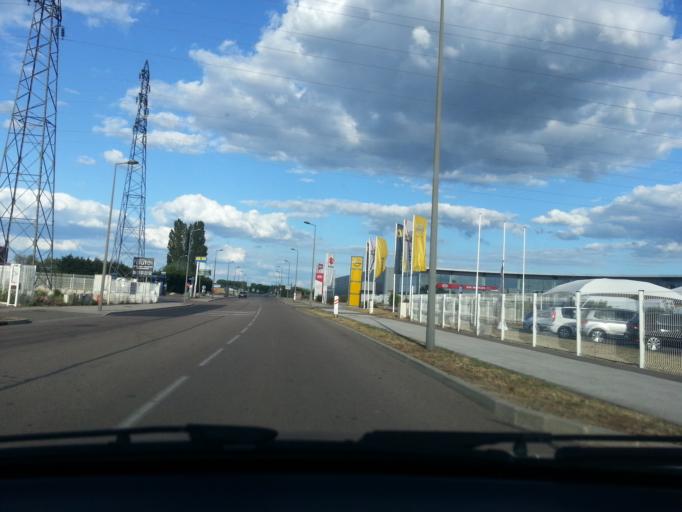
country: FR
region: Bourgogne
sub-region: Departement de Saone-et-Loire
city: Chalon-sur-Saone
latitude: 46.7685
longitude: 4.8658
